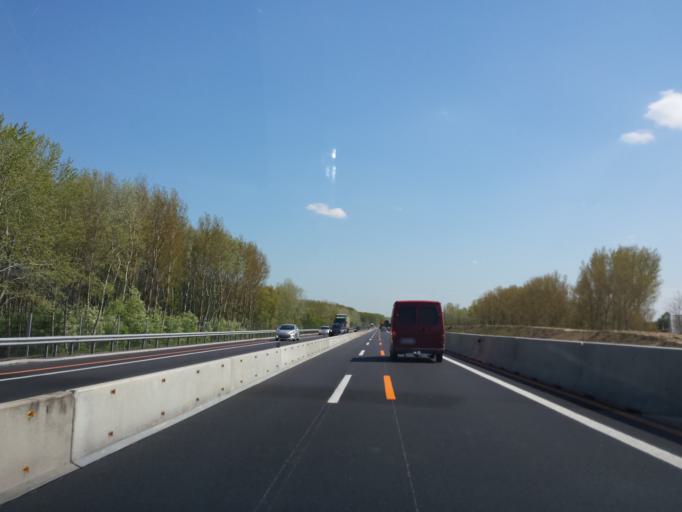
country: AT
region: Lower Austria
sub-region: Politischer Bezirk Wien-Umgebung
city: Fischamend Dorf
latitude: 48.1248
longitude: 16.6004
